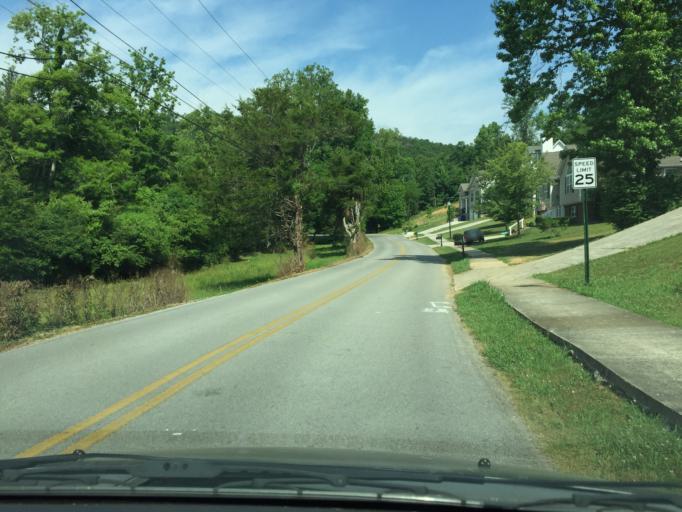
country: US
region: Tennessee
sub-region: Hamilton County
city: Collegedale
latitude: 35.0649
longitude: -85.0443
